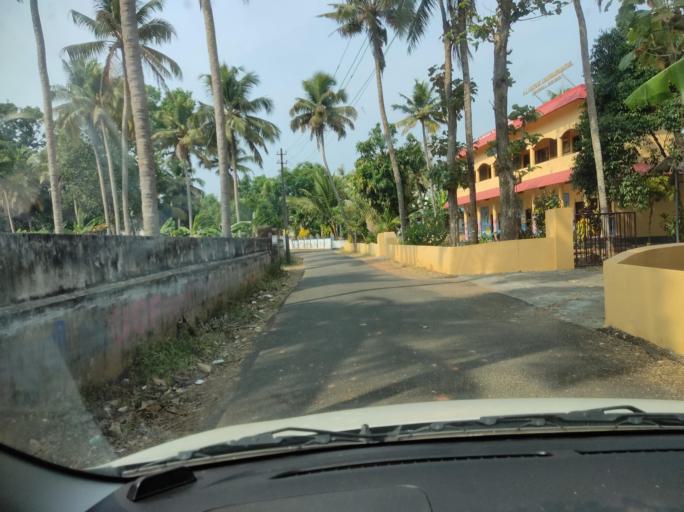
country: IN
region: Kerala
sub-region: Kottayam
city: Kottayam
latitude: 9.6864
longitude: 76.5007
